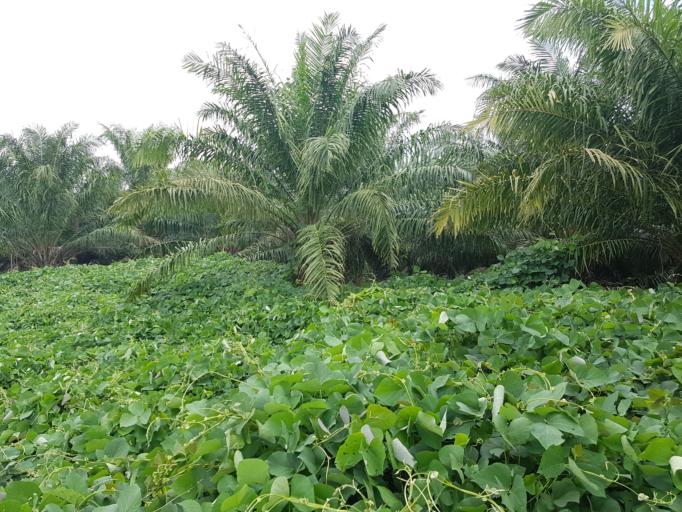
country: MX
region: Chiapas
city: Palenque
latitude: 17.6258
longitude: -91.9064
